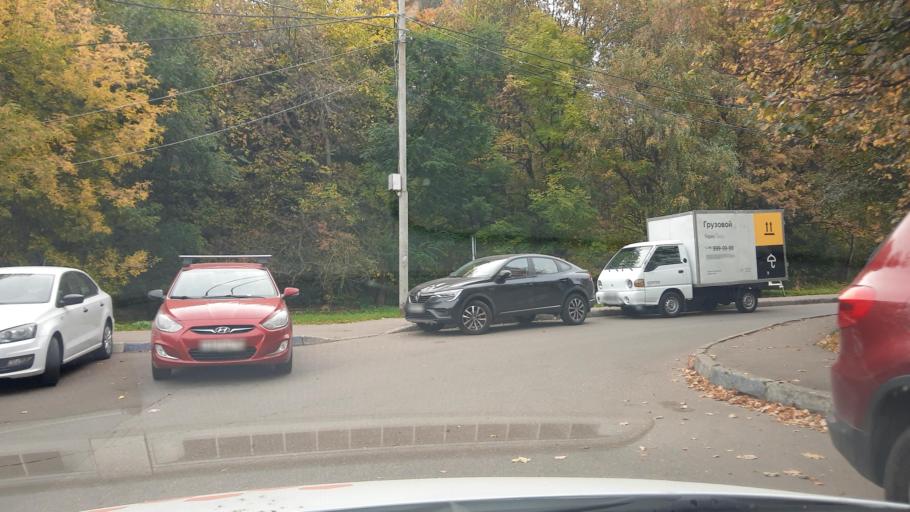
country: RU
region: Moscow
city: Yasenevo
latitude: 55.6043
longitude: 37.5551
